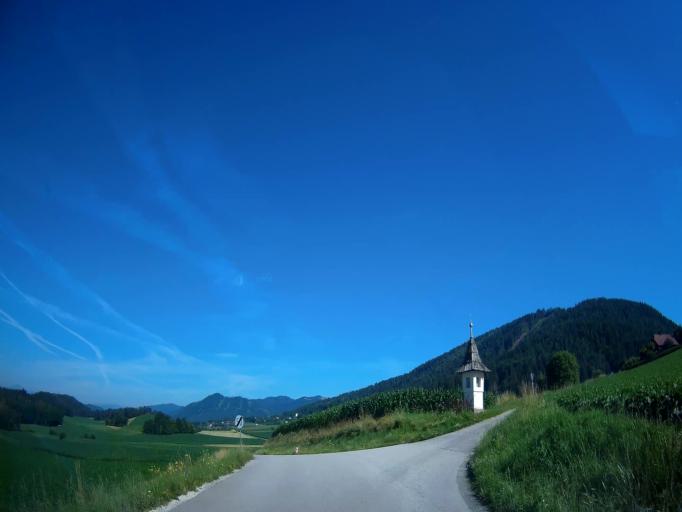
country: AT
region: Carinthia
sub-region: Politischer Bezirk Sankt Veit an der Glan
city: Bruckl
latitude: 46.6683
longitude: 14.5317
